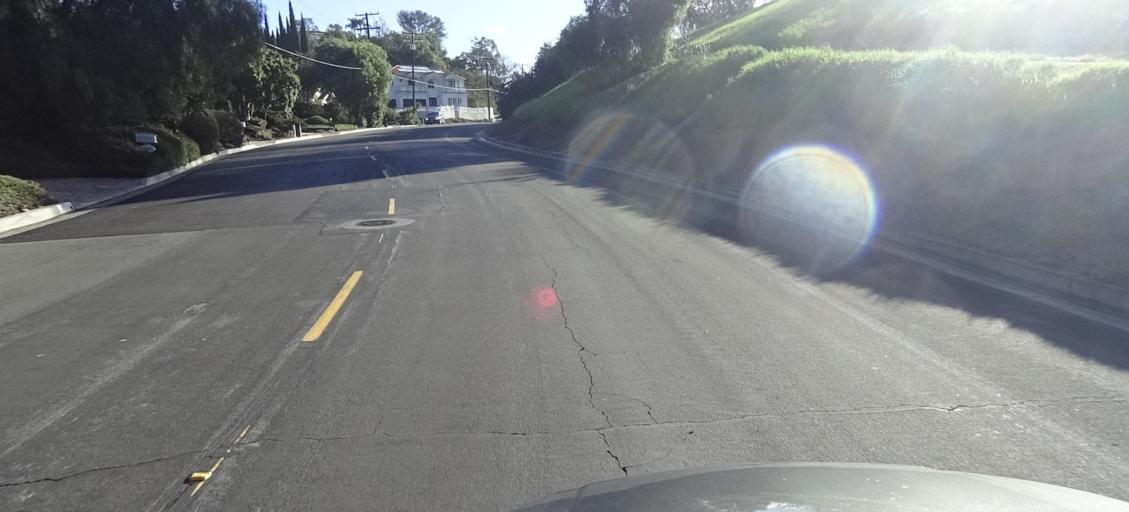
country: US
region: California
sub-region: Orange County
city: North Tustin
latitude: 33.7721
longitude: -117.7758
